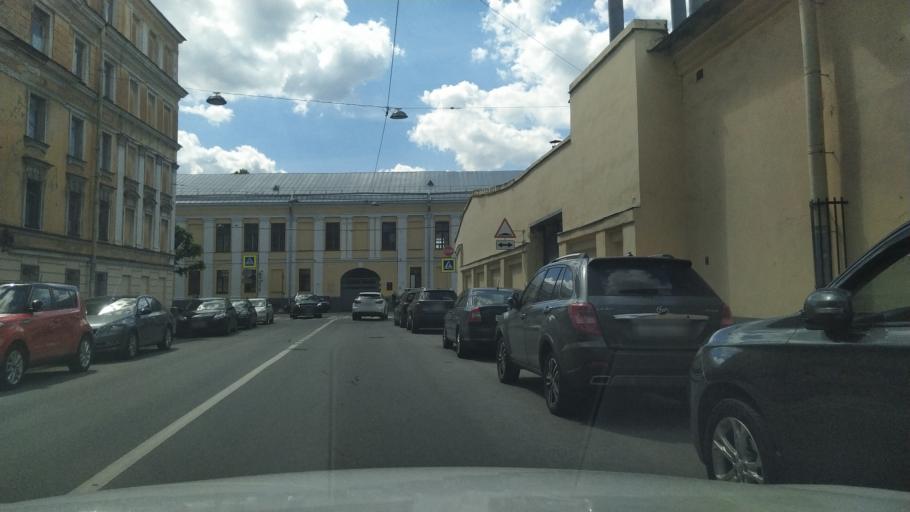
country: RU
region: St.-Petersburg
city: Petrogradka
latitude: 59.9581
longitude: 30.2869
